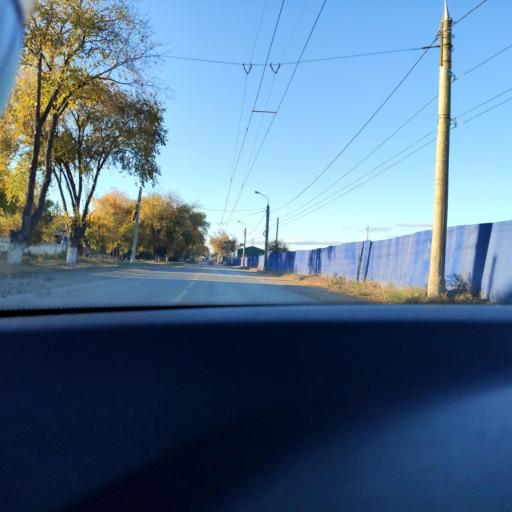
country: RU
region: Samara
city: Samara
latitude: 53.1946
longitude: 50.2729
